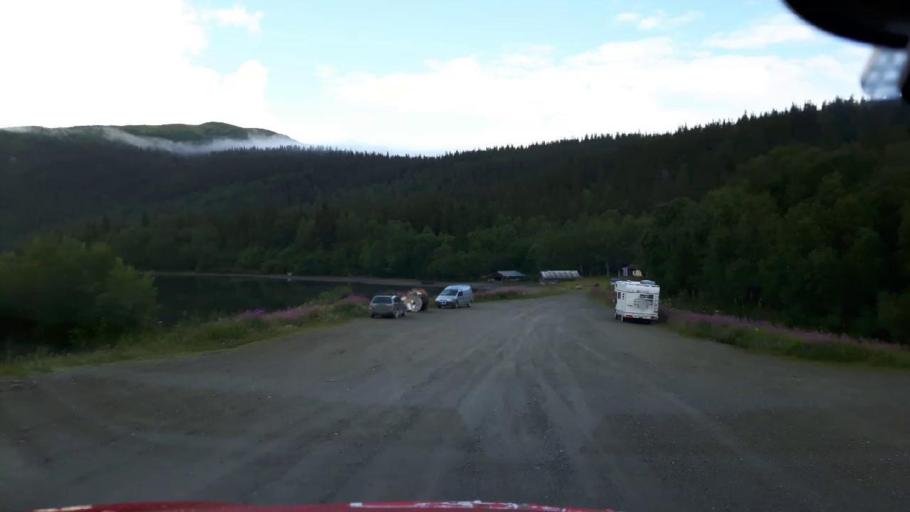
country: NO
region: Nordland
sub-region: Hattfjelldal
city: Hattfjelldal
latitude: 64.8862
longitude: 14.7636
